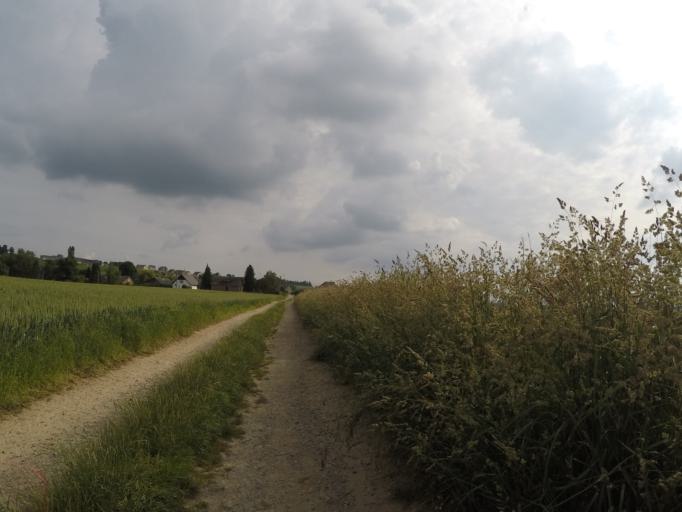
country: BE
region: Wallonia
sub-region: Province de Namur
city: Ciney
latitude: 50.3141
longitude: 5.0529
